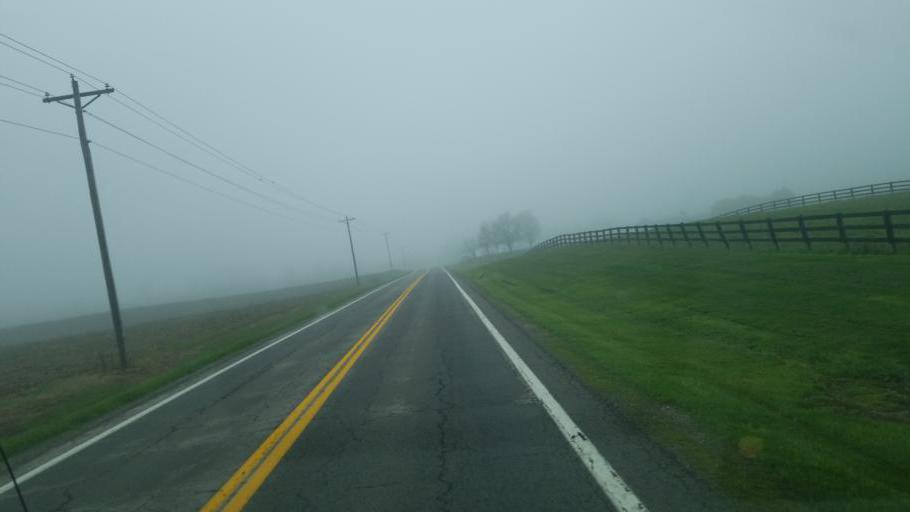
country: US
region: Ohio
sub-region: Logan County
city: Northwood
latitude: 40.4227
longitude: -83.5995
